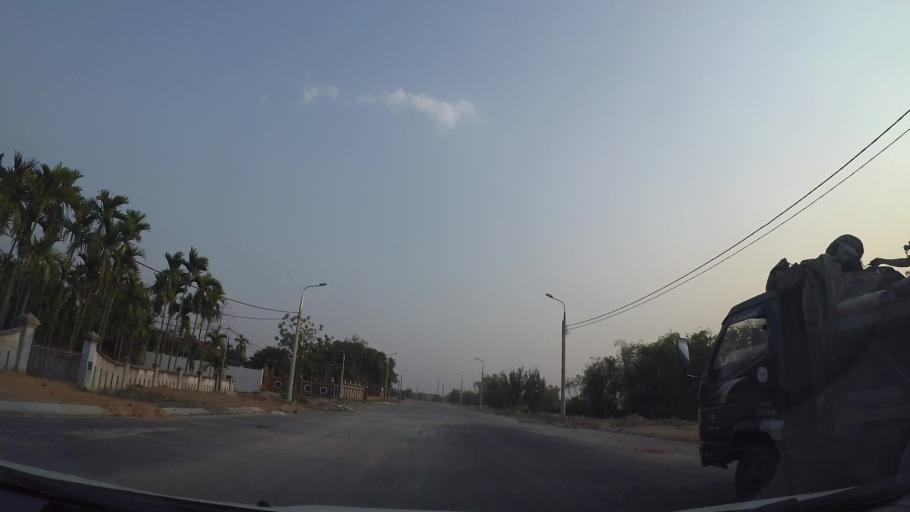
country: VN
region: Da Nang
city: Ngu Hanh Son
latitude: 15.9629
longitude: 108.2312
